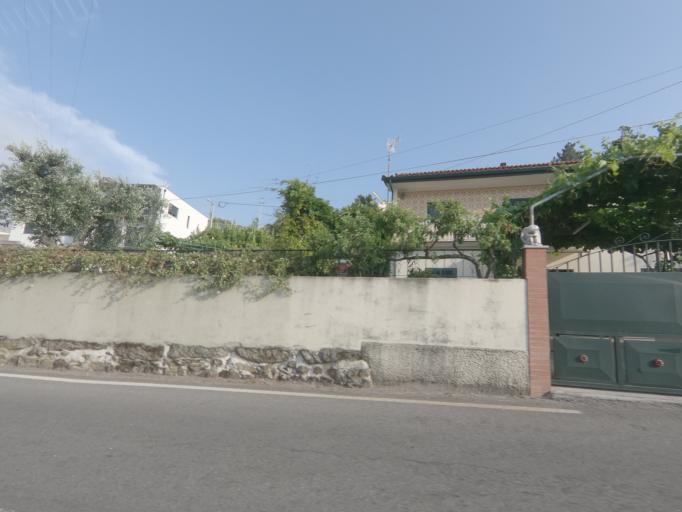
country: PT
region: Viseu
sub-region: Tabuaco
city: Tabuaco
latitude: 41.1156
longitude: -7.5718
